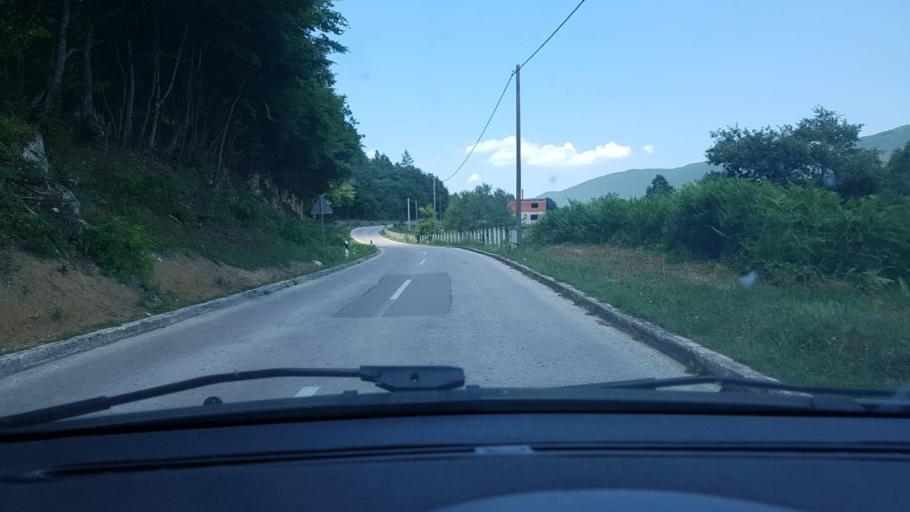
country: BA
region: Federation of Bosnia and Herzegovina
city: Orasac
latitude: 44.6047
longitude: 16.0700
